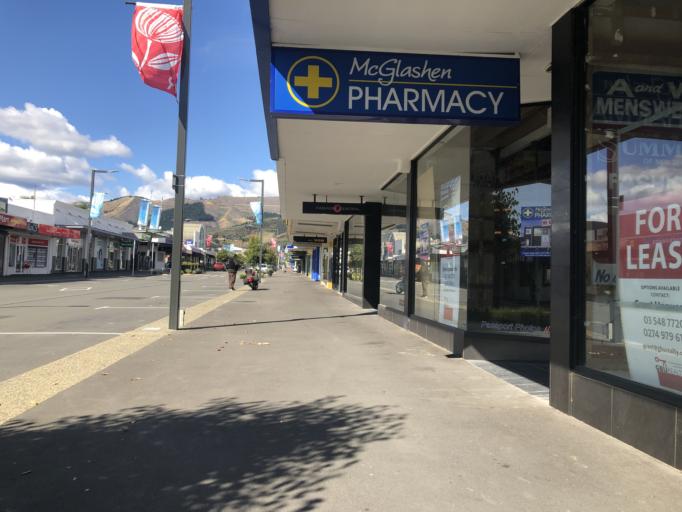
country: NZ
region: Tasman
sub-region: Tasman District
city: Richmond
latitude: -41.3394
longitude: 173.1848
